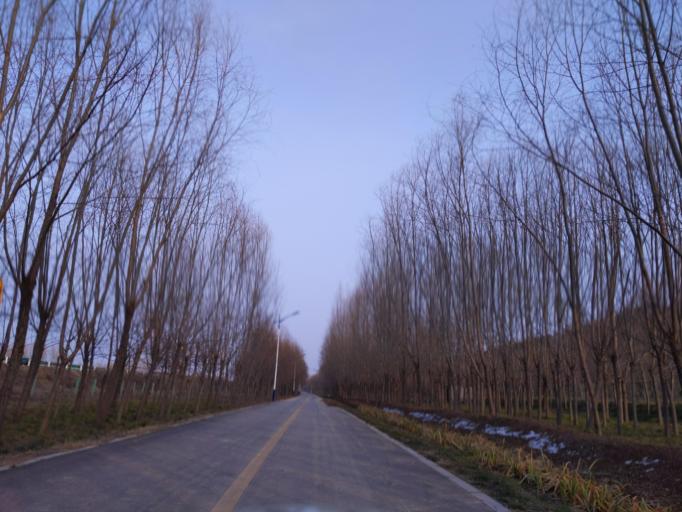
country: CN
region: Henan Sheng
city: Puyang
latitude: 35.8211
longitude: 115.0021
